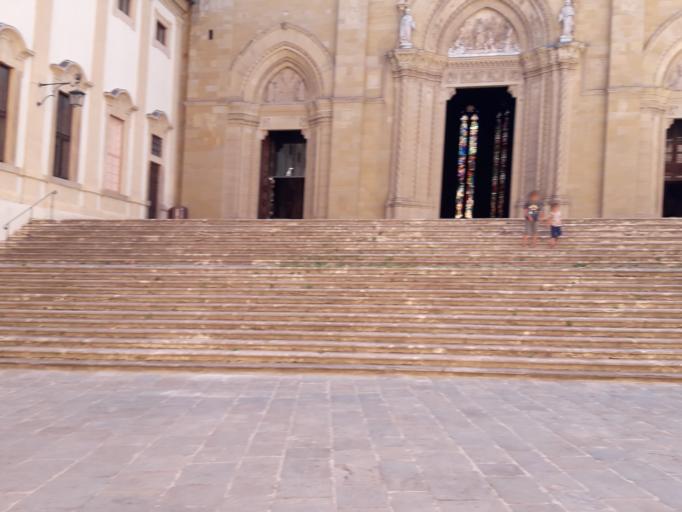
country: IT
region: Tuscany
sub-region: Province of Arezzo
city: Arezzo
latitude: 43.4672
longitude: 11.8826
